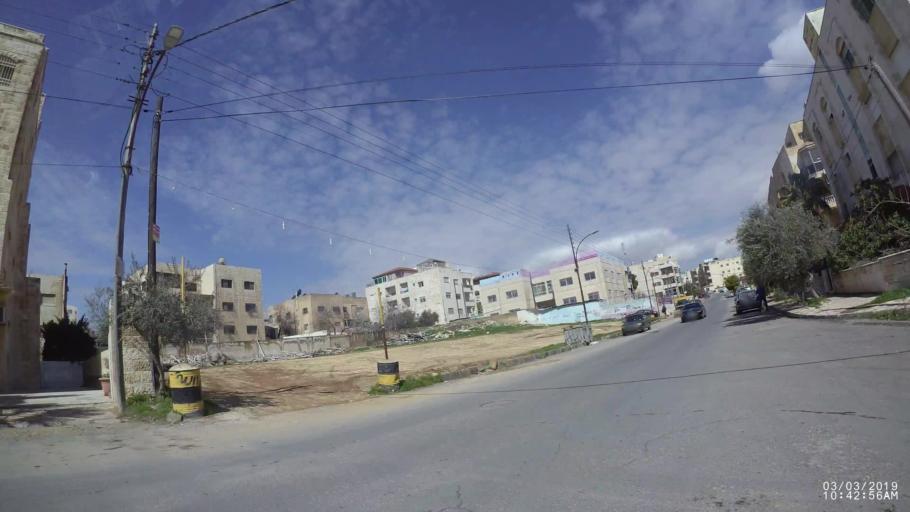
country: JO
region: Amman
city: Al Jubayhah
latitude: 31.9920
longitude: 35.9061
